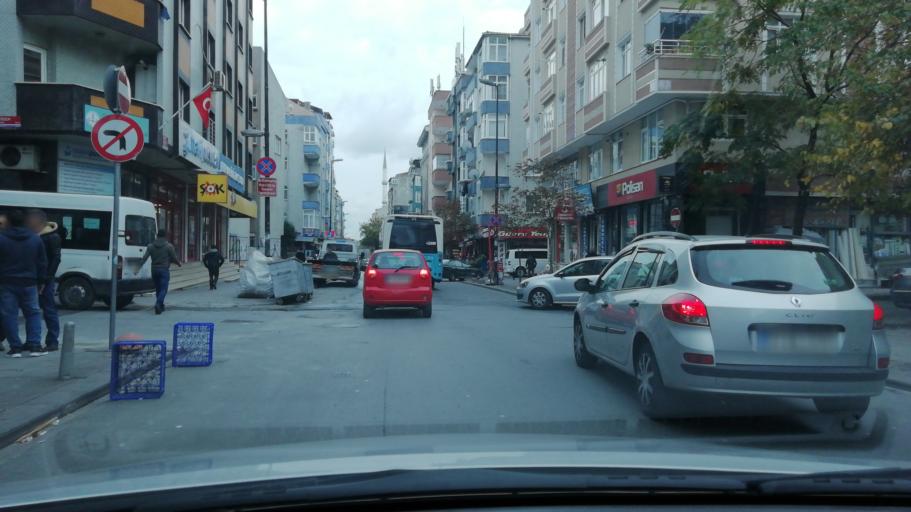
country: TR
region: Istanbul
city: Bahcelievler
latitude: 41.0068
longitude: 28.8387
